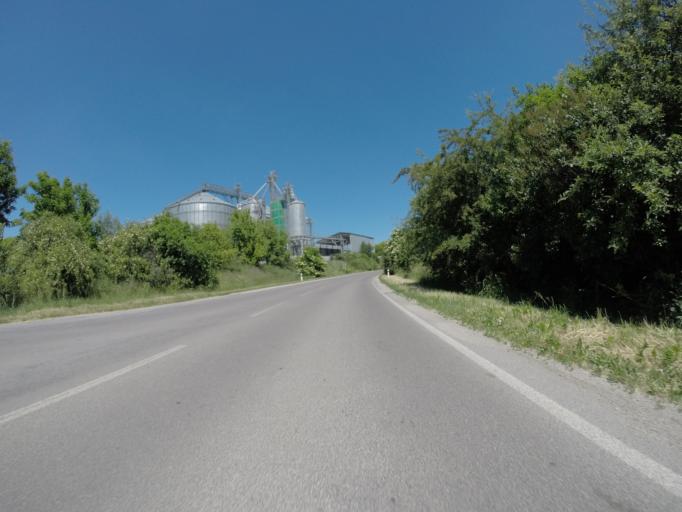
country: SK
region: Trnavsky
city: Hlohovec
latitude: 48.3797
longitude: 17.7925
